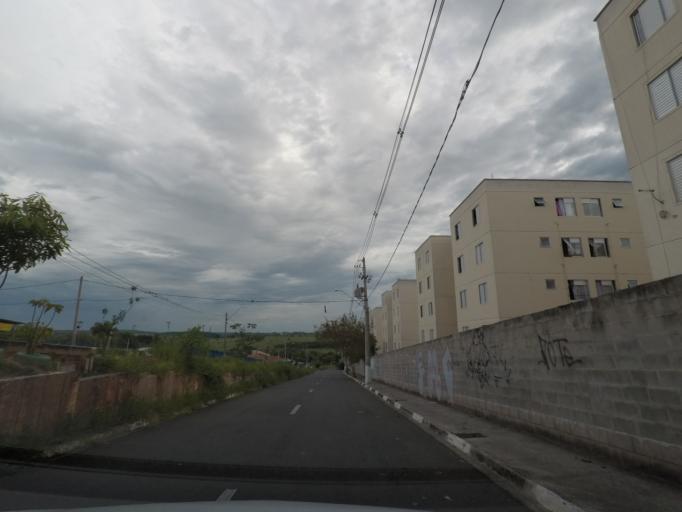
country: BR
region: Sao Paulo
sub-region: Hortolandia
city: Hortolandia
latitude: -22.9658
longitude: -47.2007
